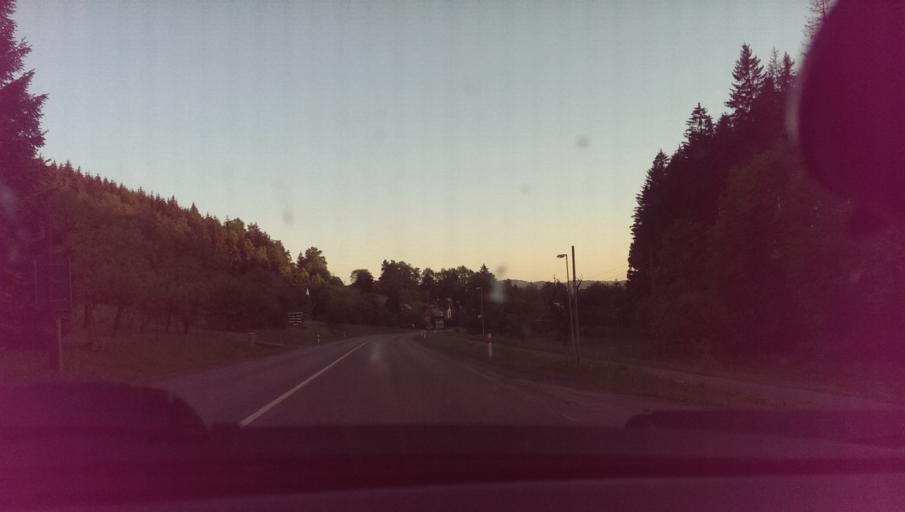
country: CZ
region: Zlin
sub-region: Okres Vsetin
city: Roznov pod Radhostem
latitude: 49.4851
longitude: 18.1702
